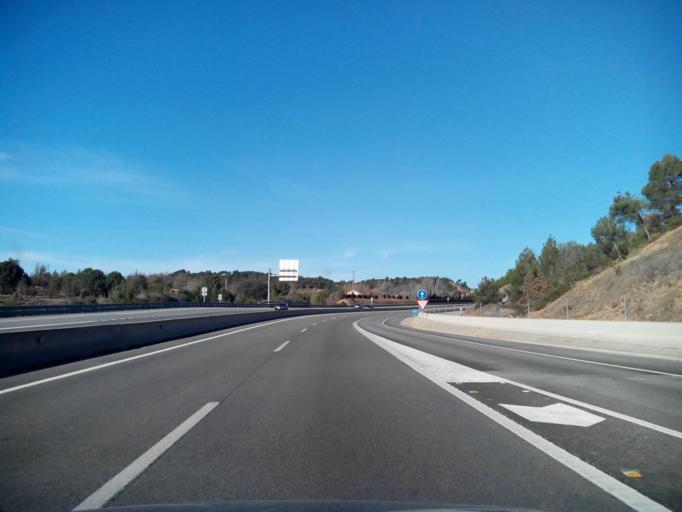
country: ES
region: Catalonia
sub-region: Provincia de Barcelona
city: Balsareny
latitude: 41.8743
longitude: 1.8764
